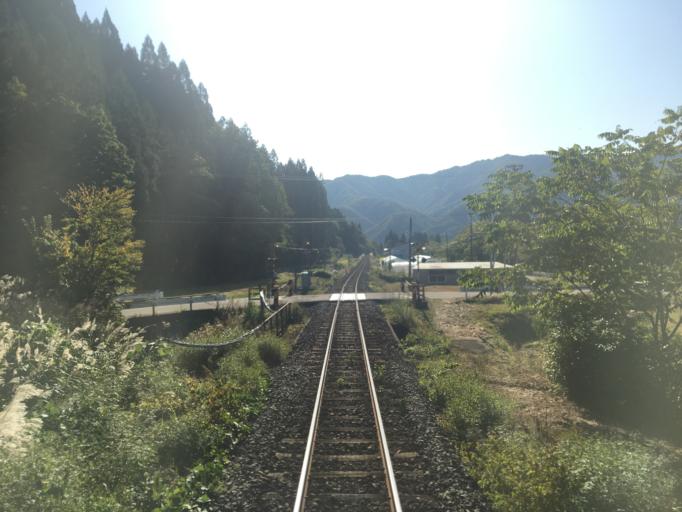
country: JP
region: Akita
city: Kakunodatemachi
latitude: 39.7319
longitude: 140.5754
